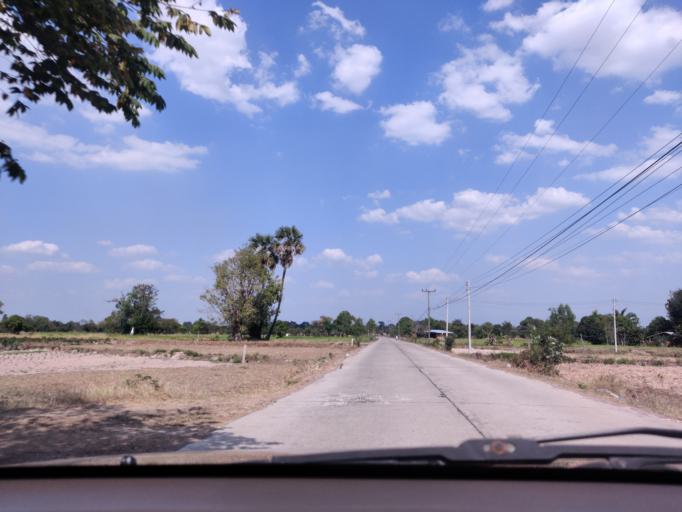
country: TH
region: Sisaket
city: Si Sa Ket
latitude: 15.0657
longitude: 104.3552
